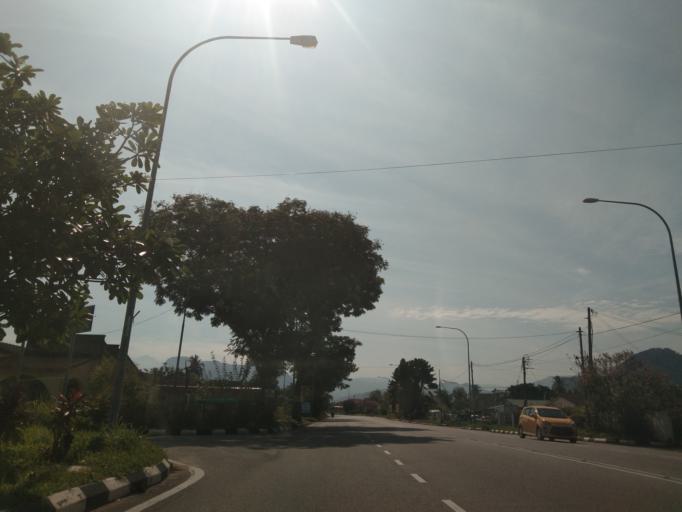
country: MY
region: Perak
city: Ipoh
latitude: 4.5677
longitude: 101.1218
